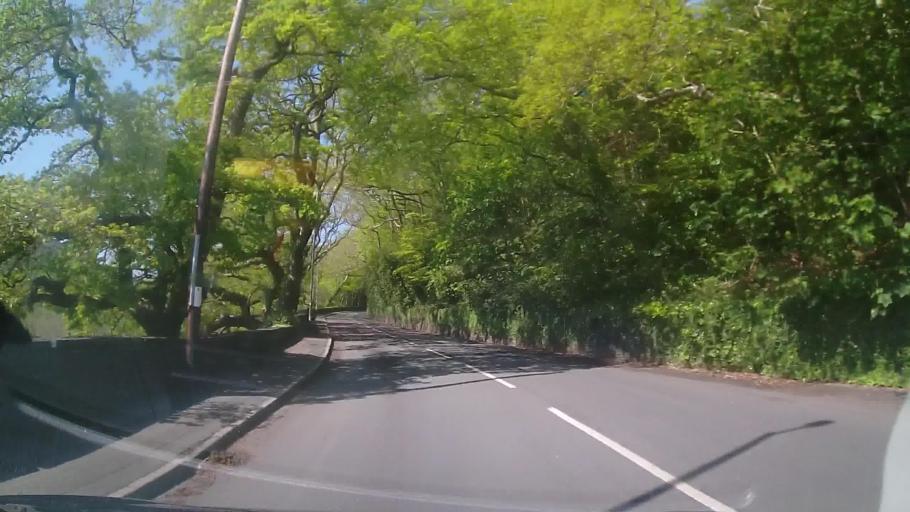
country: GB
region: Wales
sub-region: Gwynedd
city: Porthmadog
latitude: 52.9190
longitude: -4.1338
